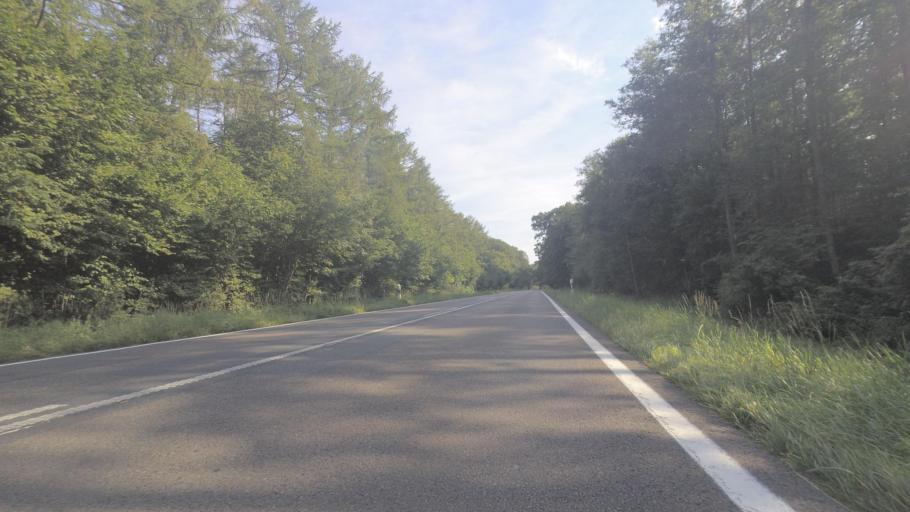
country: DE
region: Mecklenburg-Vorpommern
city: Grimmen
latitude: 54.0699
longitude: 13.1144
